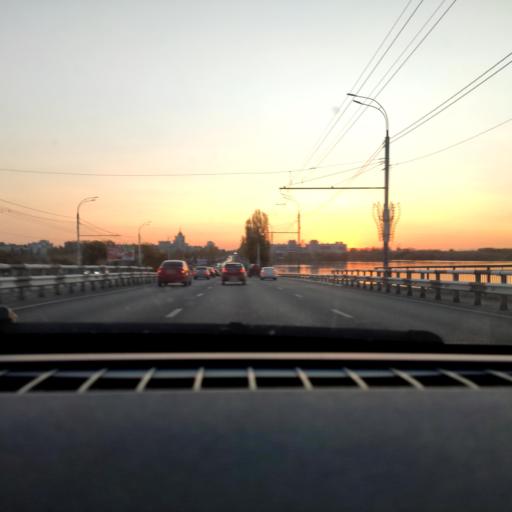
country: RU
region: Voronezj
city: Voronezh
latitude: 51.6672
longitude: 39.2274
